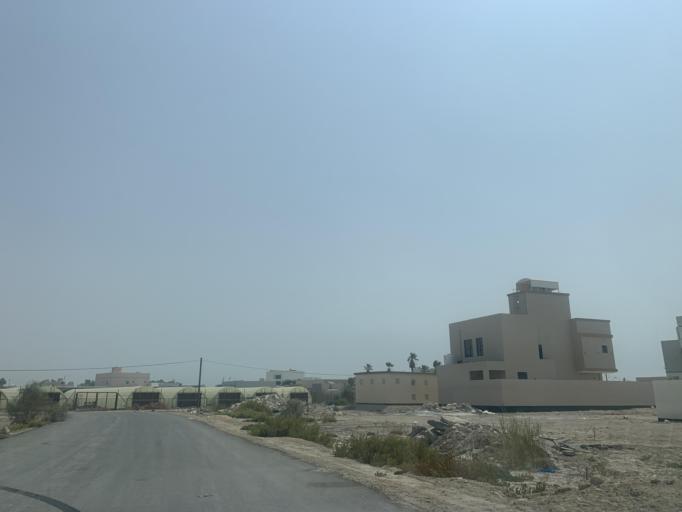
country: BH
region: Central Governorate
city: Madinat Hamad
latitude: 26.1283
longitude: 50.4699
